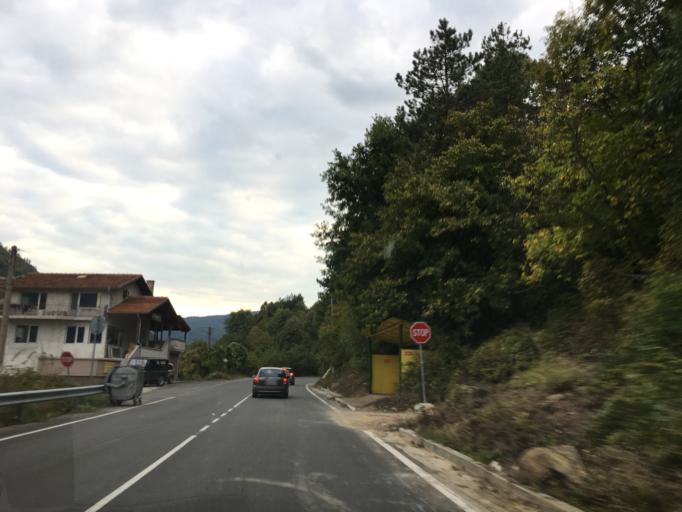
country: BG
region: Sofiya
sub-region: Obshtina Svoge
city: Svoge
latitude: 42.9787
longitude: 23.3590
